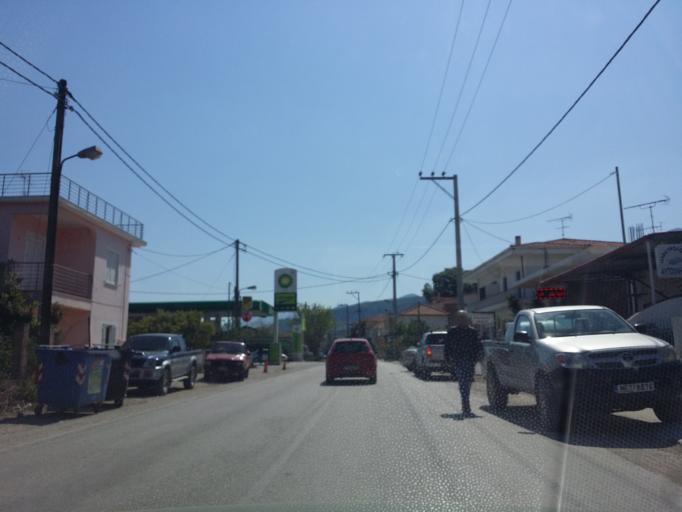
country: GR
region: West Greece
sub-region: Nomos Achaias
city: Aiyira
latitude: 38.1513
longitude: 22.3494
